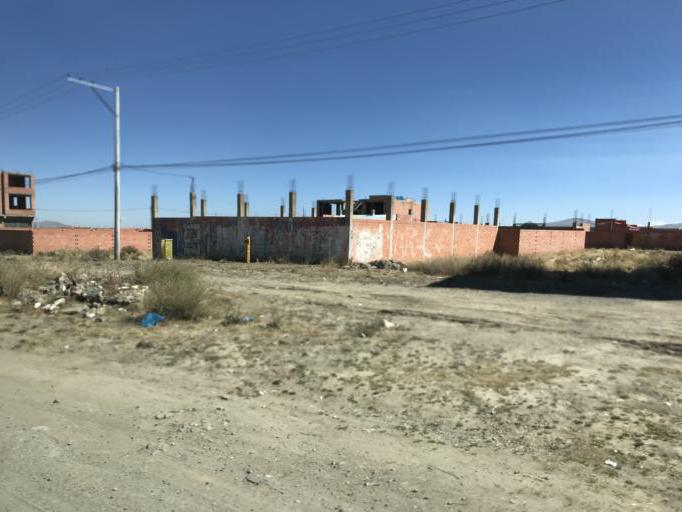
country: BO
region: La Paz
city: La Paz
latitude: -16.5084
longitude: -68.2637
